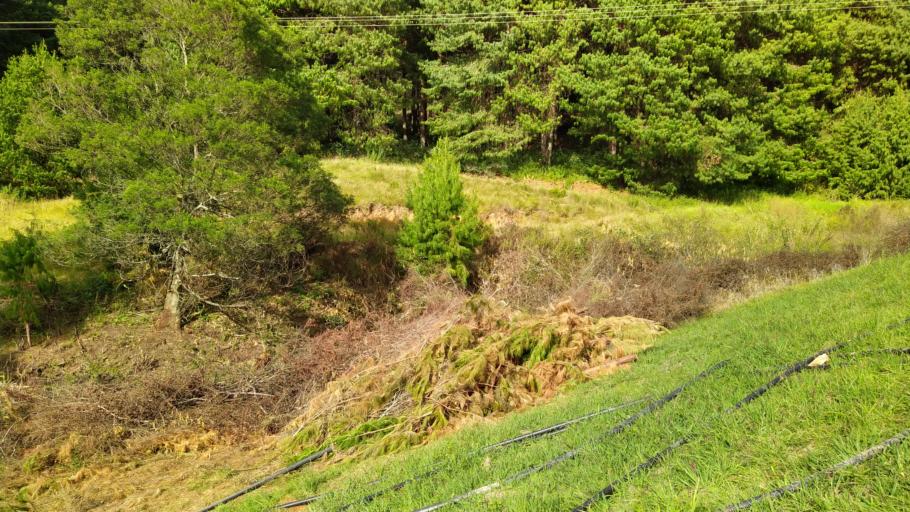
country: ZA
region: KwaZulu-Natal
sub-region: uMgungundlovu District Municipality
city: Mooirivier
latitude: -29.3595
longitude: 29.9776
